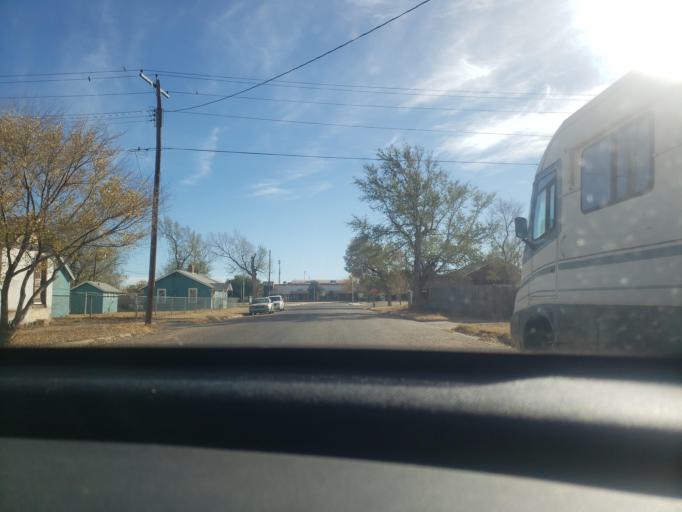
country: US
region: Kansas
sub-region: Finney County
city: Garden City
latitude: 37.9787
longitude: -100.8714
